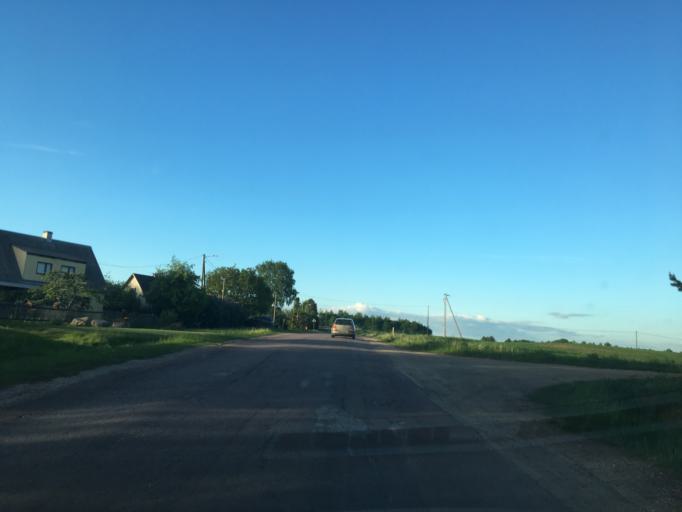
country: EE
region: Tartu
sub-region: Elva linn
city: Elva
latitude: 58.2182
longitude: 26.4353
